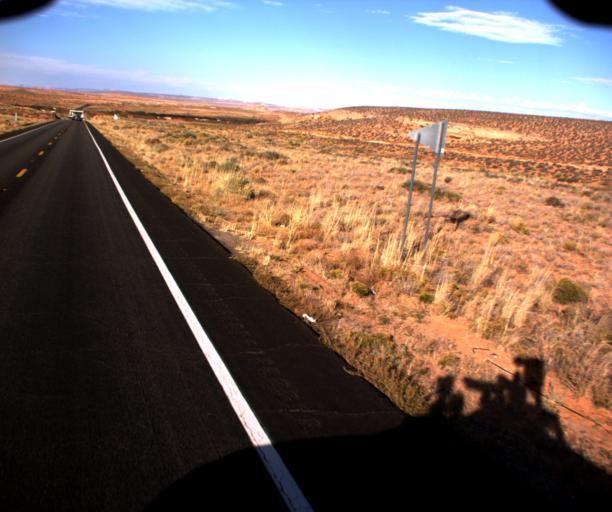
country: US
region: Arizona
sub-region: Apache County
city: Many Farms
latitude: 36.9252
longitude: -109.5926
